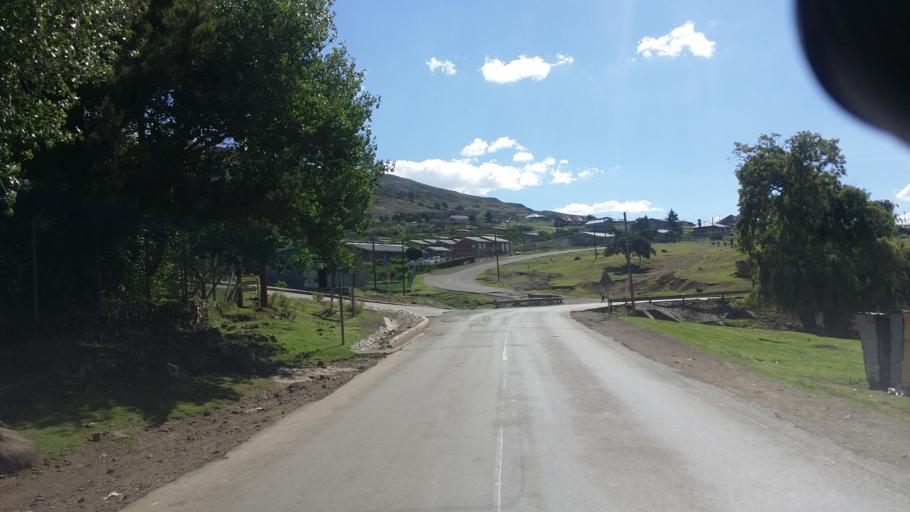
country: LS
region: Mokhotlong
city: Mokhotlong
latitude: -29.2902
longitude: 29.0736
